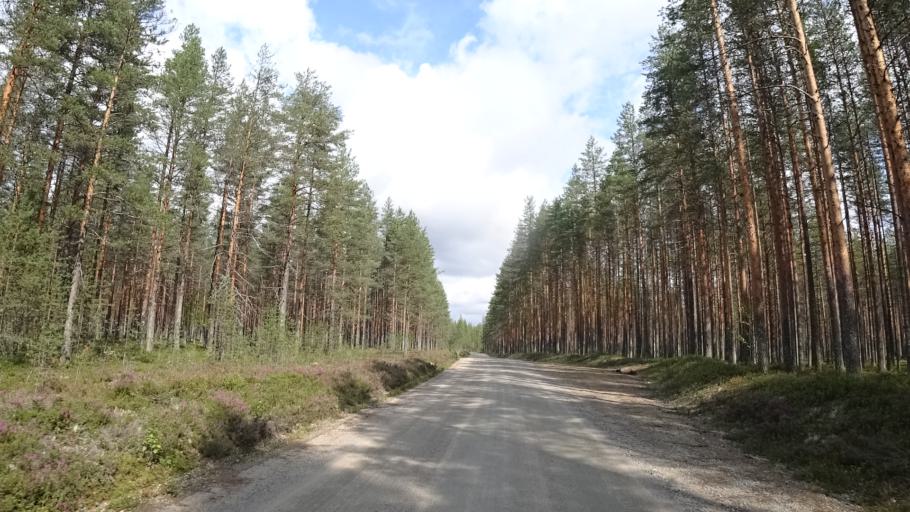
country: FI
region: North Karelia
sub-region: Joensuu
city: Ilomantsi
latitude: 62.9351
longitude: 31.4301
